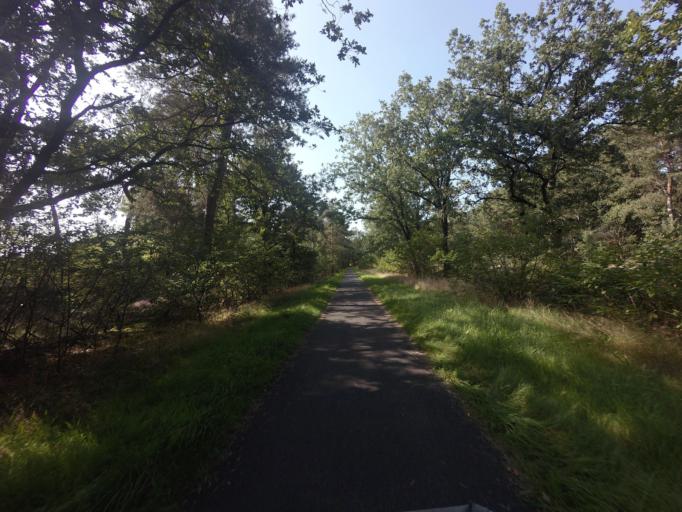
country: DE
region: Lower Saxony
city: Itterbeck
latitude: 52.5109
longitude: 6.7815
